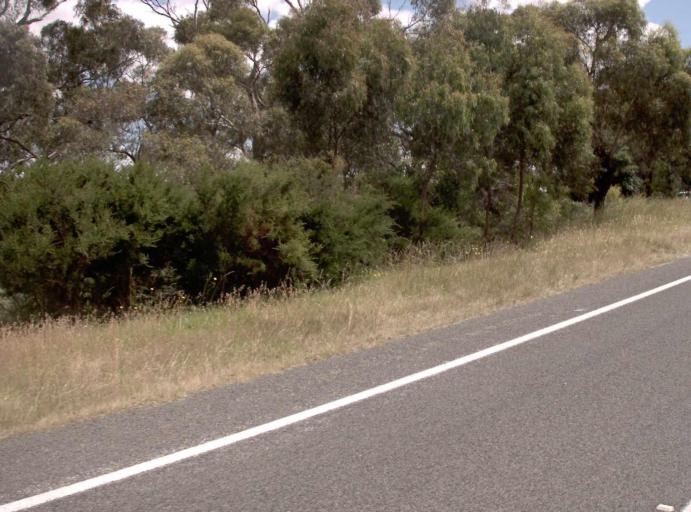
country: AU
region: Victoria
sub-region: Cardinia
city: Koo-Wee-Rup
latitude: -38.3931
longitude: 145.5401
